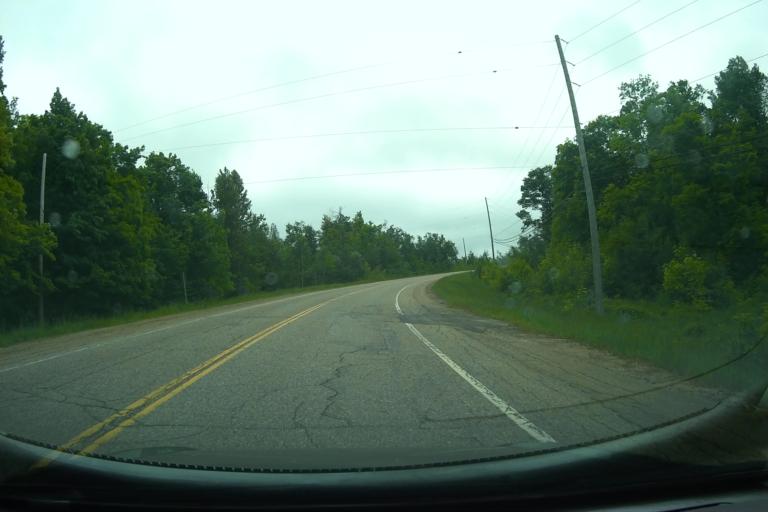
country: CA
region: Ontario
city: Pembroke
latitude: 45.4443
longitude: -77.2929
